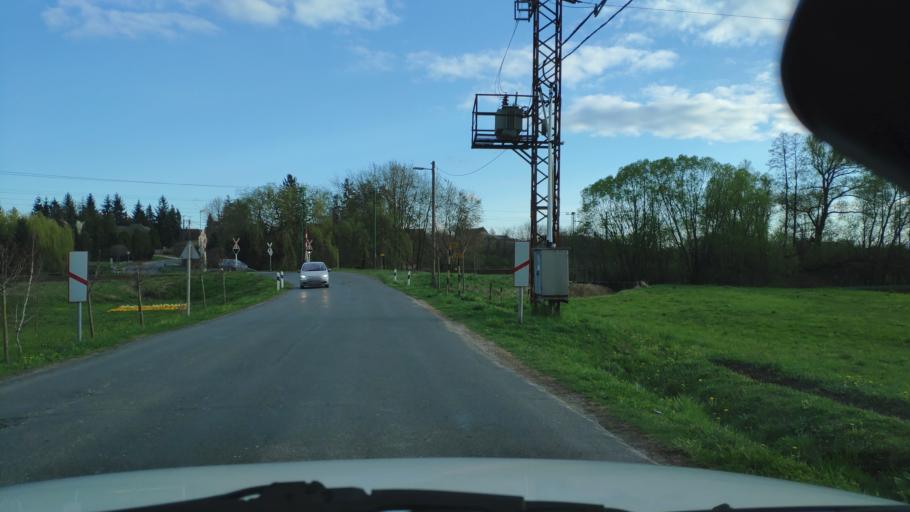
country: HU
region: Zala
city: Zalakomar
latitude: 46.4883
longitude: 17.1291
